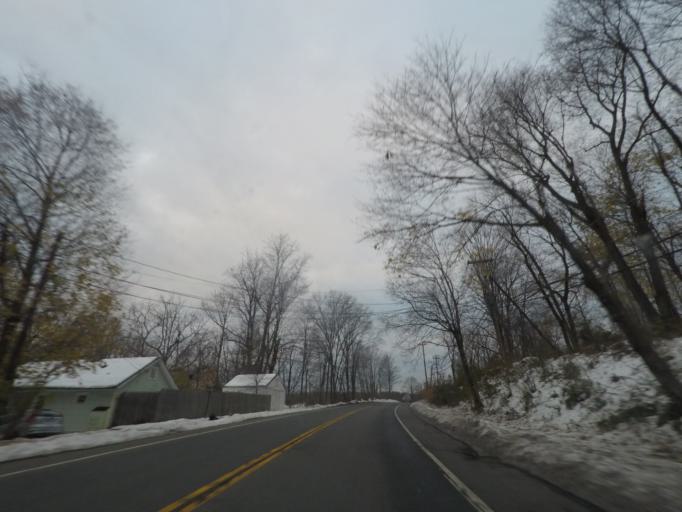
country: US
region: New York
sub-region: Orange County
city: New Windsor
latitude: 41.4950
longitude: -74.0459
